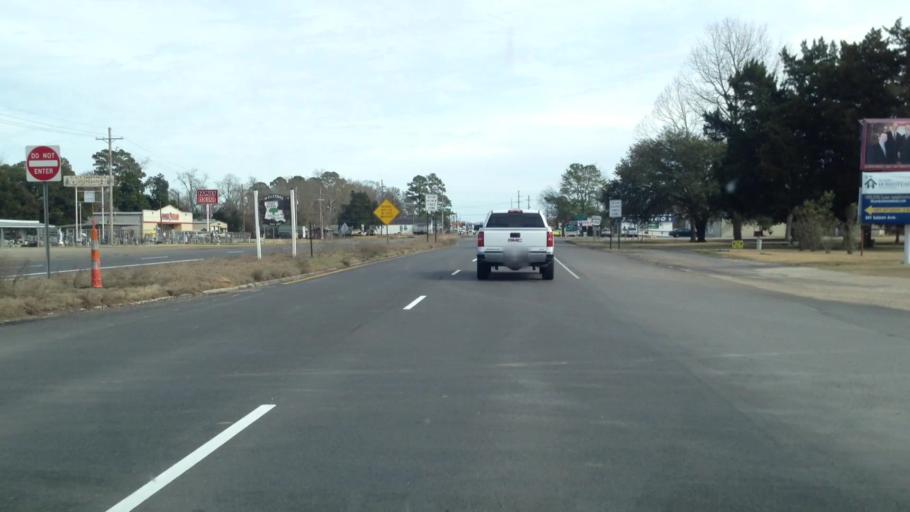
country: US
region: Louisiana
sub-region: Saint Landry Parish
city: Port Barre
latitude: 30.5468
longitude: -91.9709
